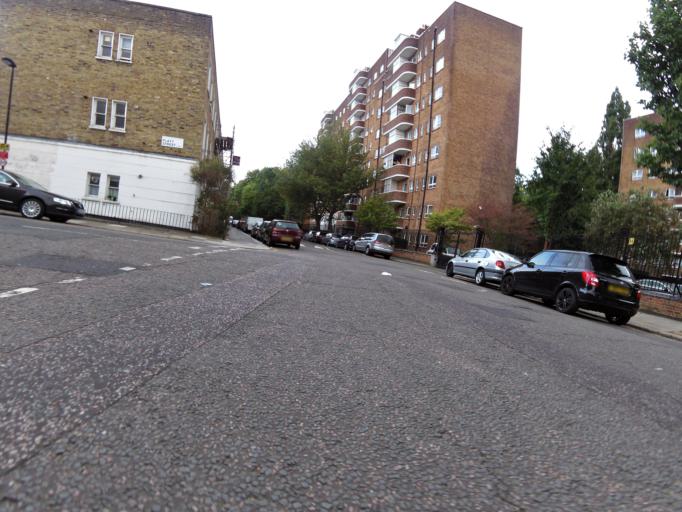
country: GB
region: England
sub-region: Greater London
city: Camden Town
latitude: 51.5338
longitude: -0.1309
